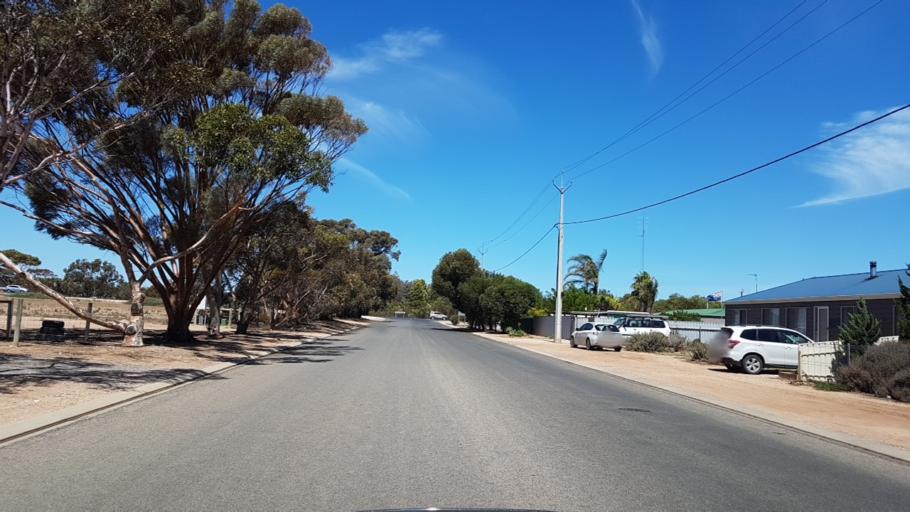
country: AU
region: South Australia
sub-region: Copper Coast
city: Wallaroo
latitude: -34.0586
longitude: 137.5837
